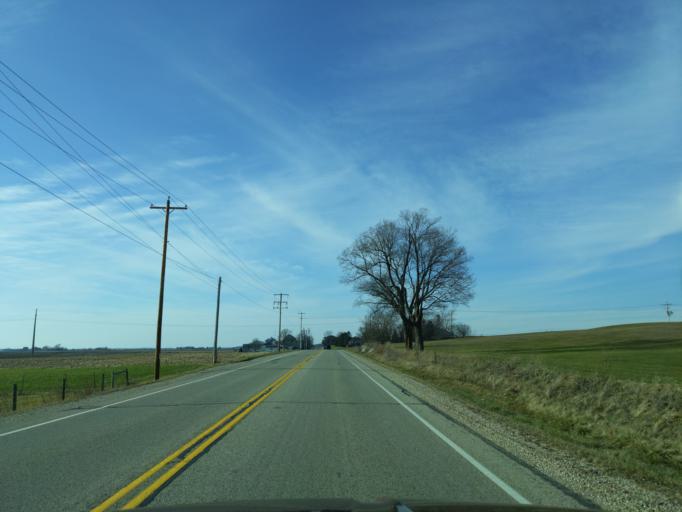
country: US
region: Wisconsin
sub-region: Walworth County
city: Elkhorn
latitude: 42.7350
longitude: -88.5897
